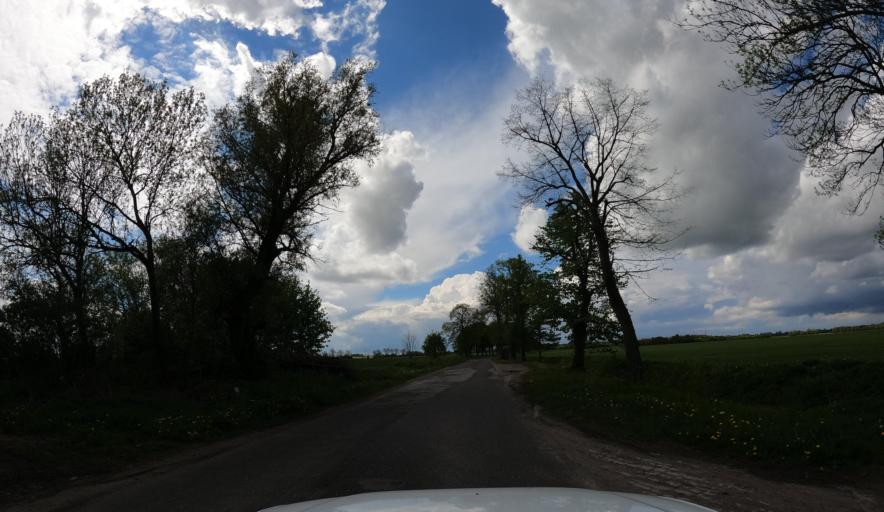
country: PL
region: West Pomeranian Voivodeship
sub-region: Powiat kamienski
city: Wolin
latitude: 53.8665
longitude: 14.6490
